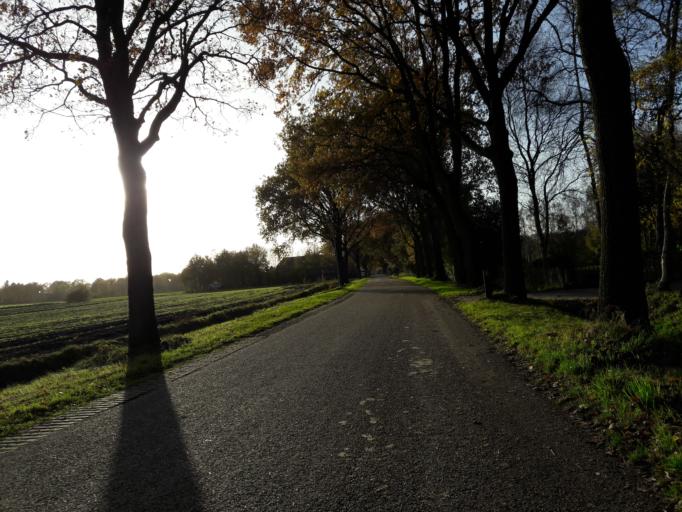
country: NL
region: Drenthe
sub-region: Gemeente Aa en Hunze
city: Anloo
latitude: 52.9399
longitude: 6.6792
